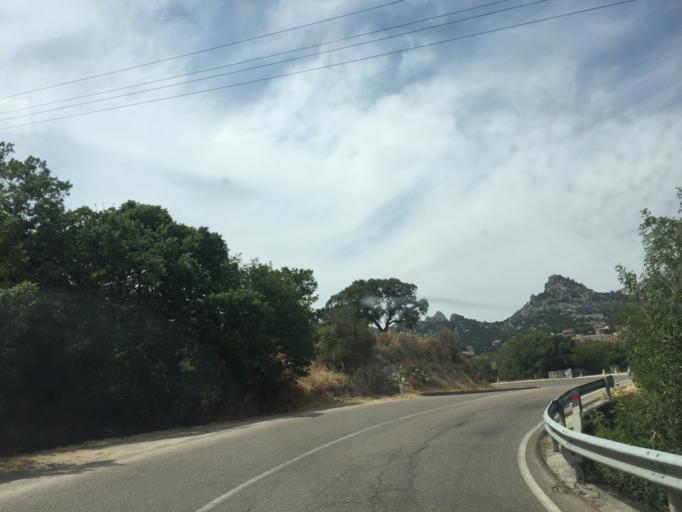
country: IT
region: Sardinia
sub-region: Provincia di Olbia-Tempio
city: Aggius
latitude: 40.9228
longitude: 9.0701
